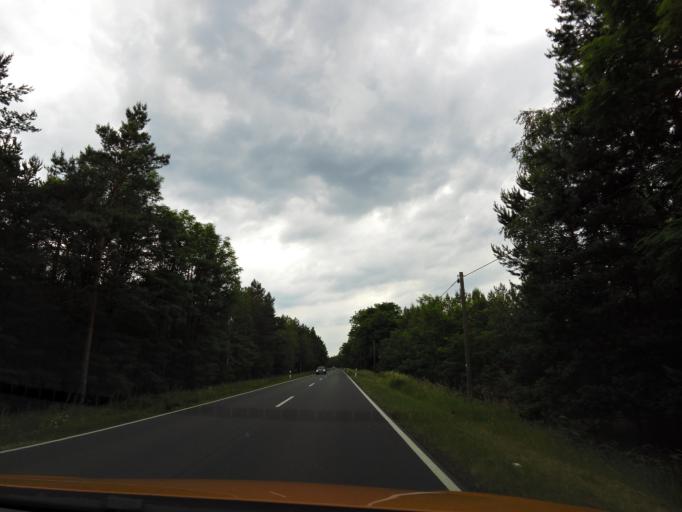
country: DE
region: Brandenburg
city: Baruth
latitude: 52.0269
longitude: 13.5356
